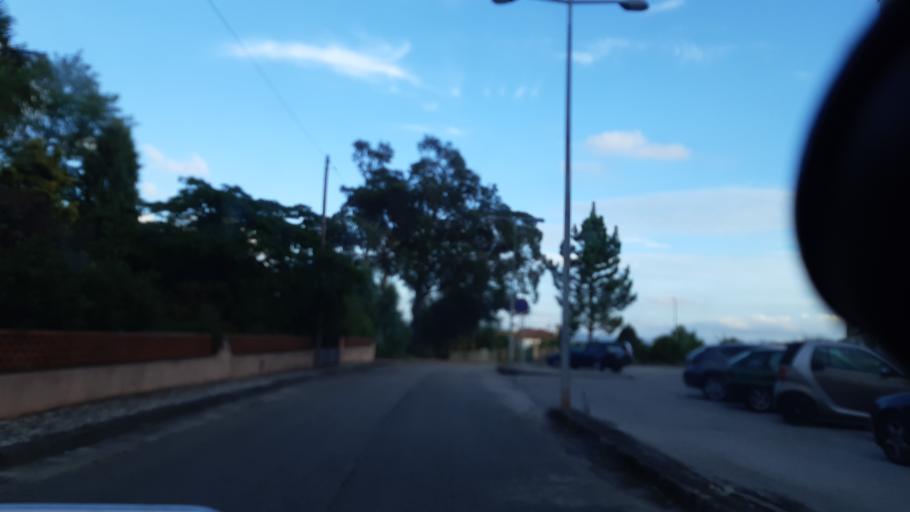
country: PT
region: Aveiro
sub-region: Agueda
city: Agueda
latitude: 40.5789
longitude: -8.4591
